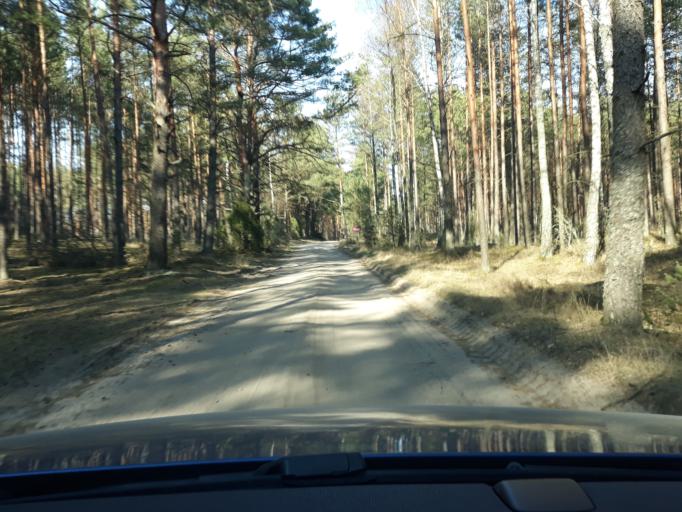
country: PL
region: Pomeranian Voivodeship
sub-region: Powiat bytowski
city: Lipnica
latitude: 53.9087
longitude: 17.4269
